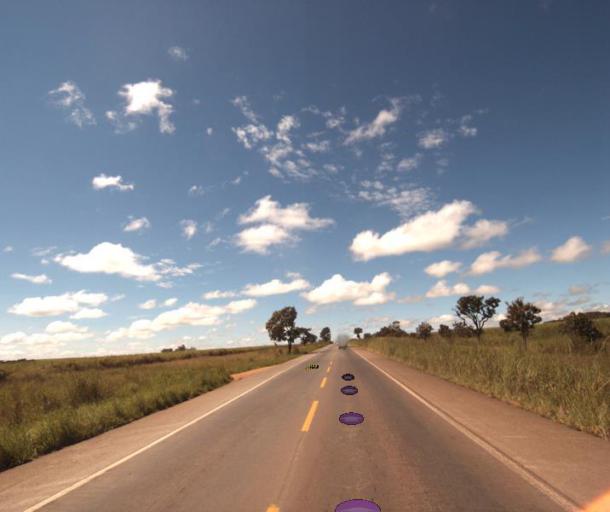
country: BR
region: Goias
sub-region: Rialma
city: Rialma
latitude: -15.4187
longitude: -49.5206
